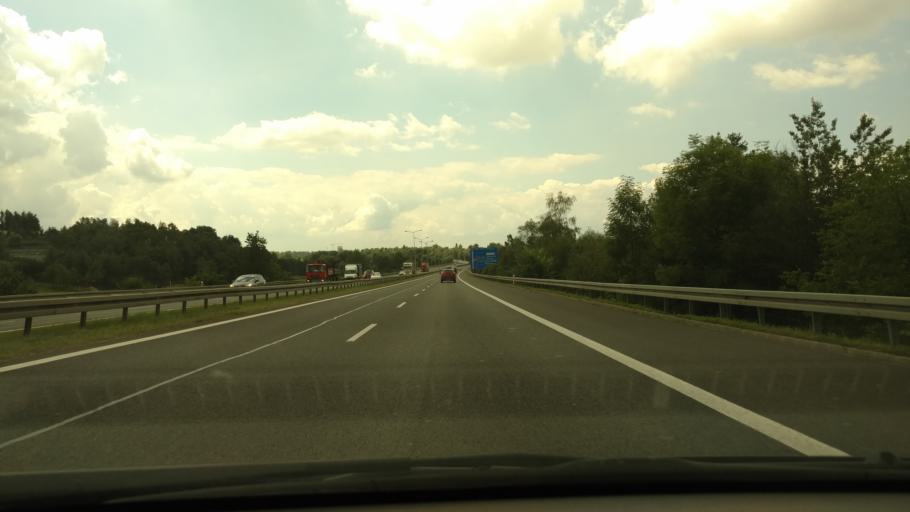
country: PL
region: Lesser Poland Voivodeship
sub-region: Powiat krakowski
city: Balice
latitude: 50.0925
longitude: 19.8149
